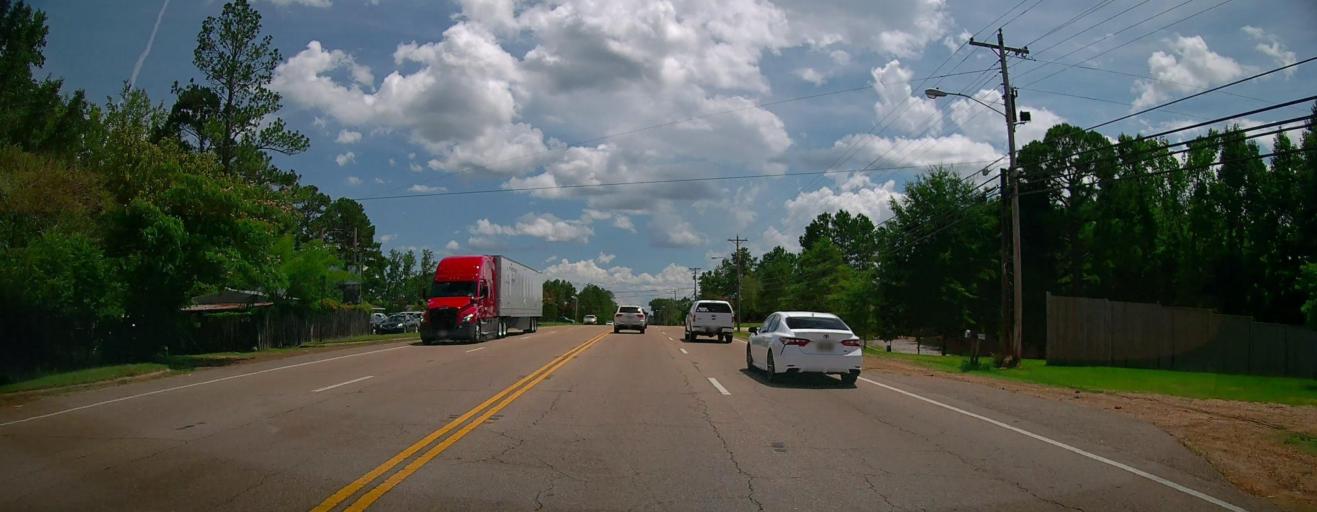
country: US
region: Mississippi
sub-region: Lee County
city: Verona
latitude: 34.1836
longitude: -88.7199
